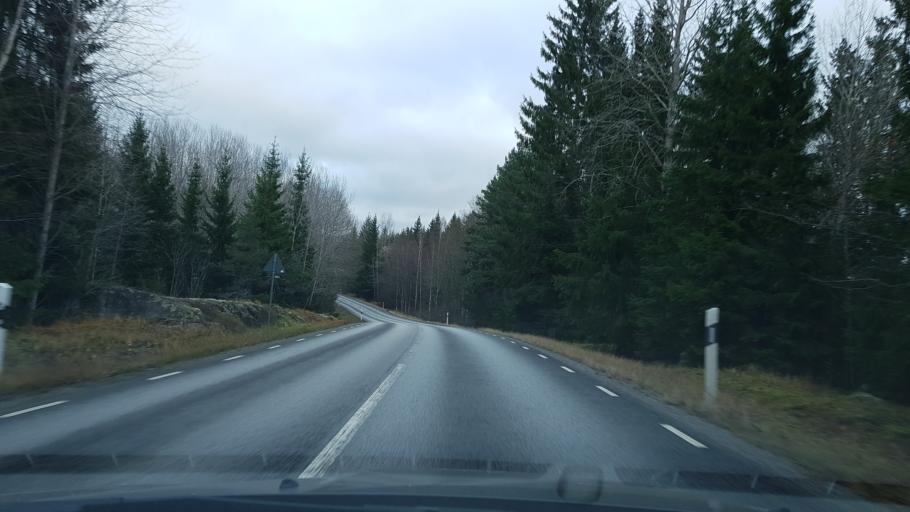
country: SE
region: Stockholm
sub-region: Norrtalje Kommun
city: Skanninge
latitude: 60.0338
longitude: 18.4708
